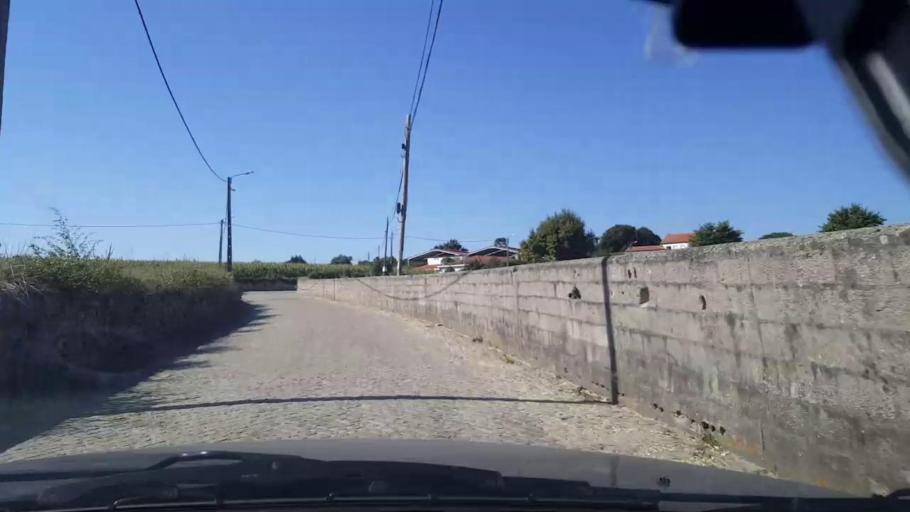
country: PT
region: Braga
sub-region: Vila Nova de Famalicao
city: Ribeirao
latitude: 41.3600
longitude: -8.6360
